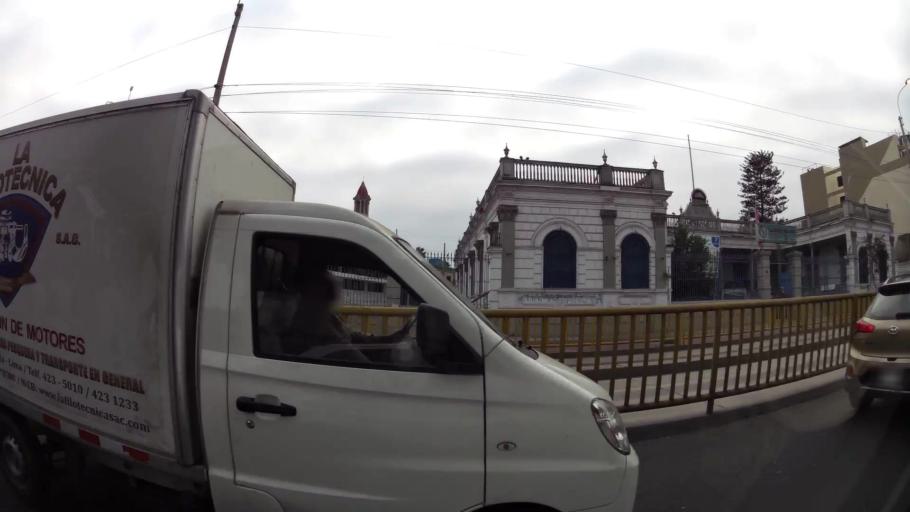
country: PE
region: Lima
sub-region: Lima
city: Surco
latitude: -12.1456
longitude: -77.0190
